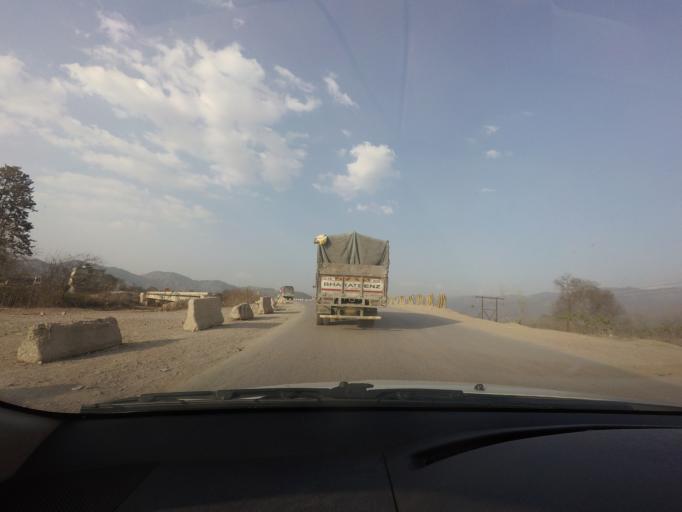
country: IN
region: Himachal Pradesh
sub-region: Mandi
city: Sundarnagar
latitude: 31.5969
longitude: 76.9244
